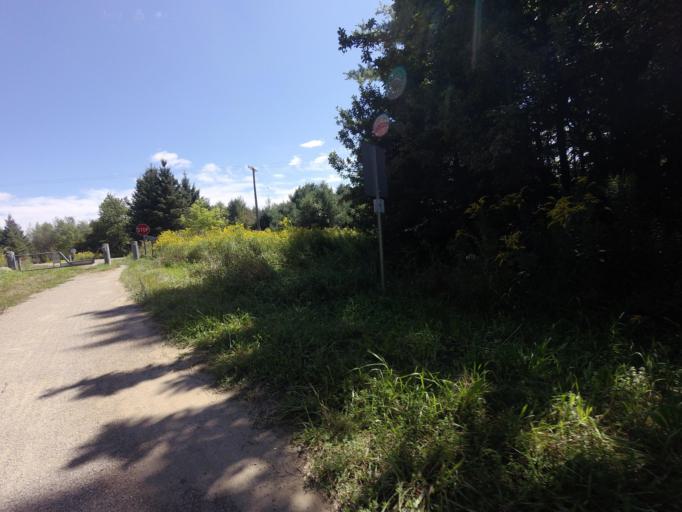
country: CA
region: Ontario
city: Orangeville
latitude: 43.7732
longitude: -80.1893
